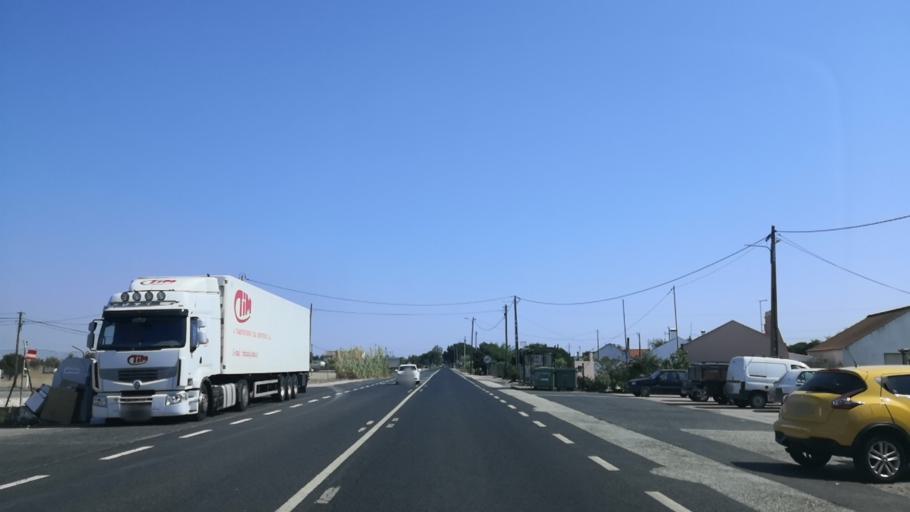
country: PT
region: Santarem
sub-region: Benavente
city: Poceirao
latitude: 38.7433
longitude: -8.6606
